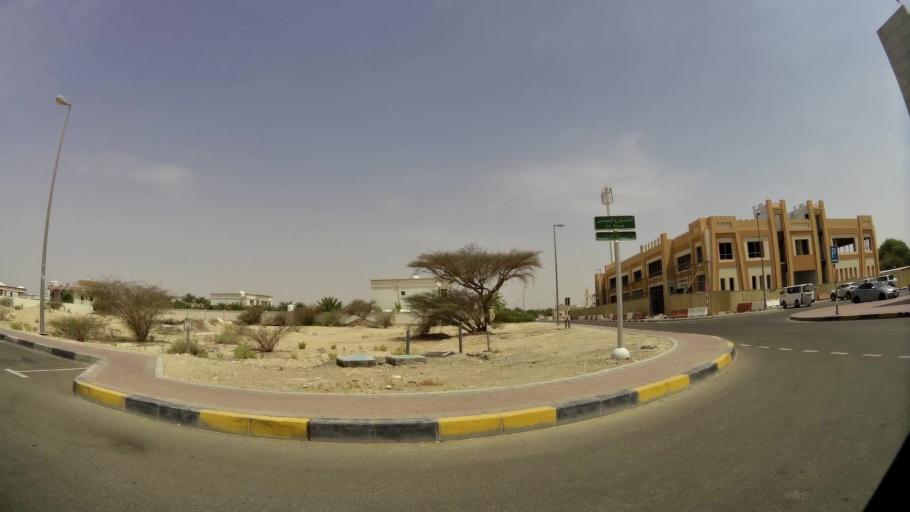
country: AE
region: Abu Dhabi
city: Al Ain
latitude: 24.1824
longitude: 55.7320
